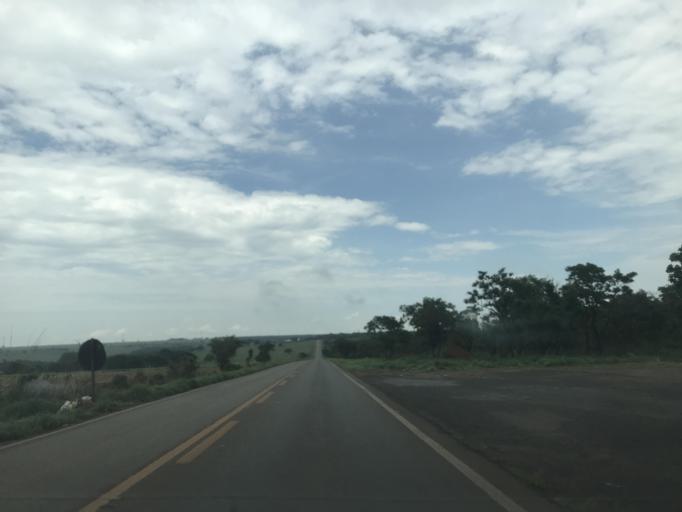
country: BR
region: Goias
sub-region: Luziania
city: Luziania
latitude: -16.2672
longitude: -47.9815
